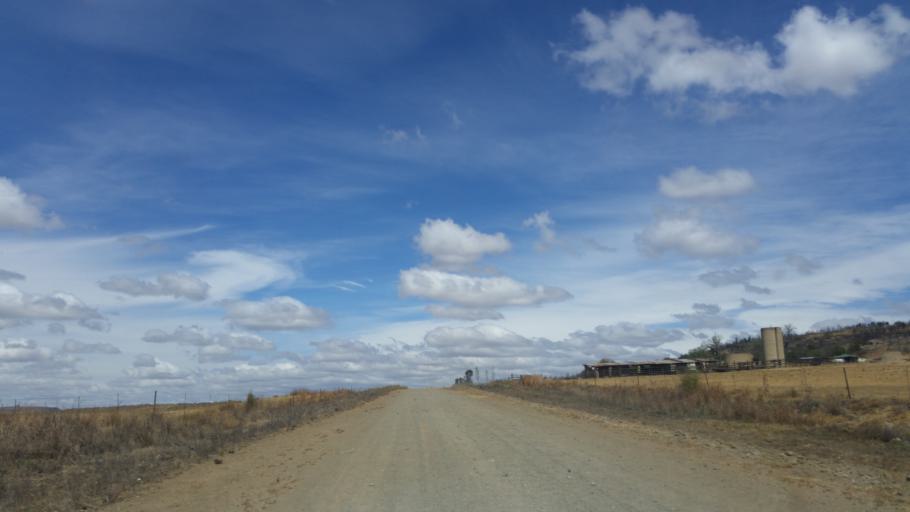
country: ZA
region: Orange Free State
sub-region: Thabo Mofutsanyana District Municipality
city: Bethlehem
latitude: -28.2481
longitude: 28.5836
